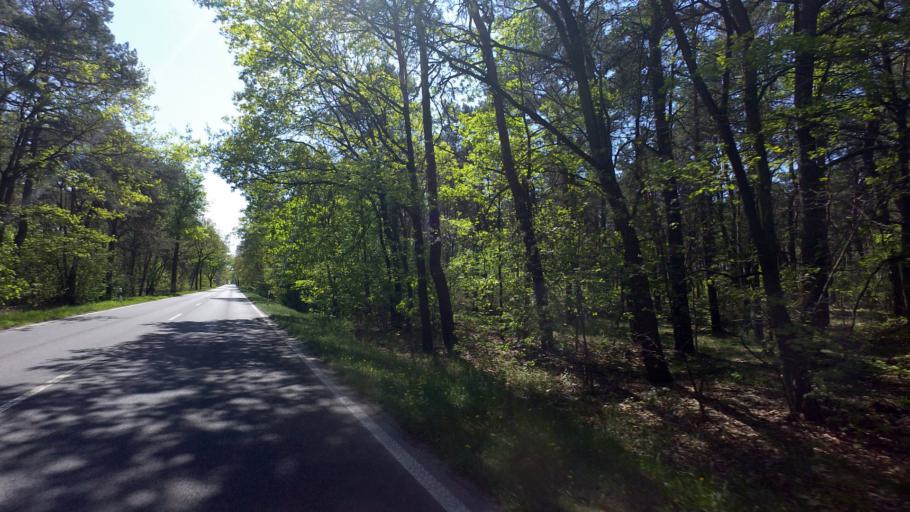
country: DE
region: Brandenburg
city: Bestensee
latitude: 52.2525
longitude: 13.6560
